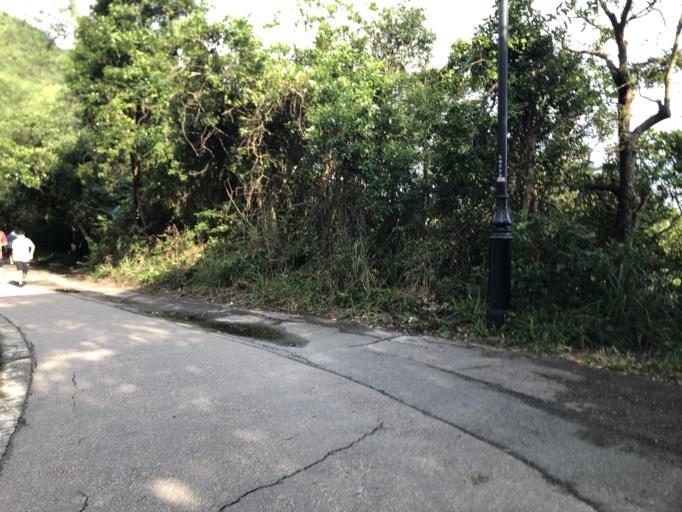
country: HK
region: Central and Western
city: Central
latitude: 22.2727
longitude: 114.1397
